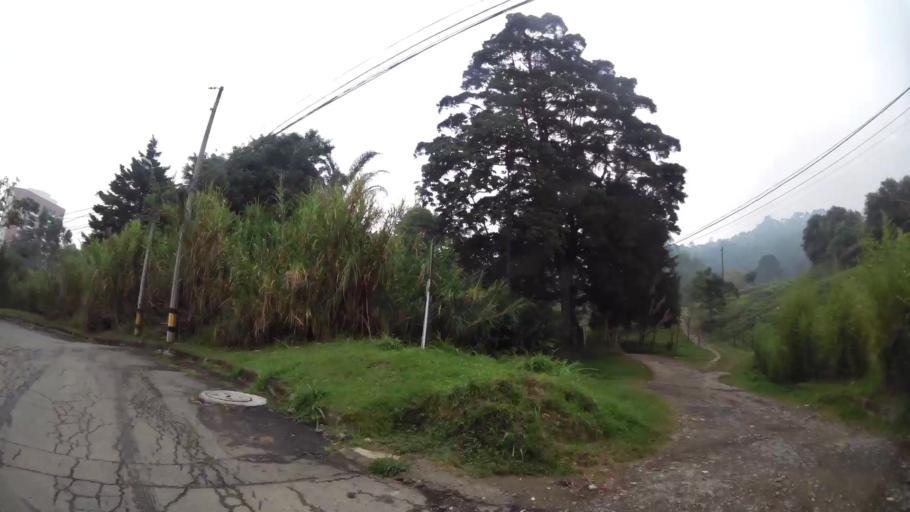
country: CO
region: Antioquia
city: Envigado
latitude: 6.1942
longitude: -75.5527
